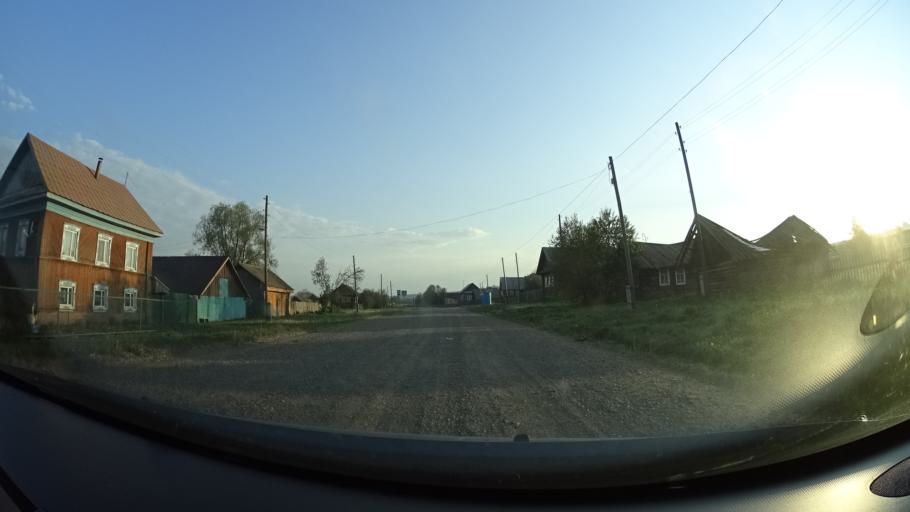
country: RU
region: Perm
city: Kuyeda
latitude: 56.6653
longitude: 55.6938
